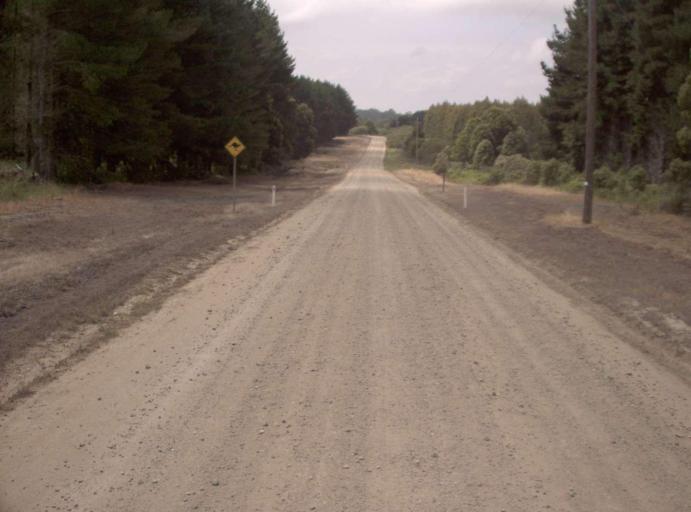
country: AU
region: Victoria
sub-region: Latrobe
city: Traralgon
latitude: -38.3967
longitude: 146.6576
